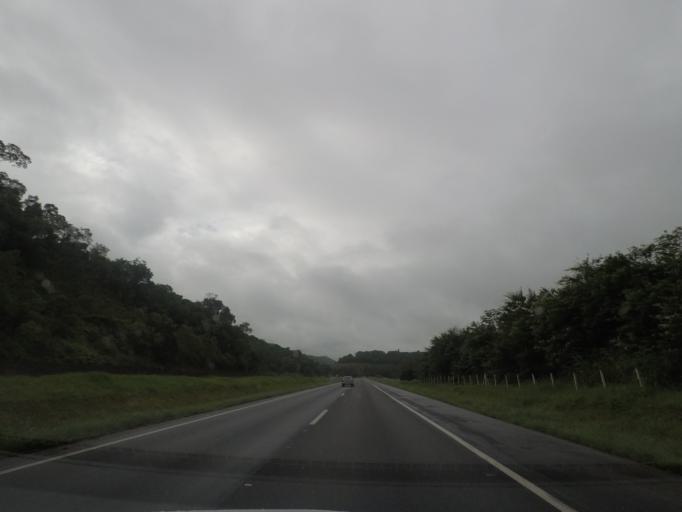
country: BR
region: Sao Paulo
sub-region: Juquia
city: Juquia
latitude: -24.3792
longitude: -47.7122
